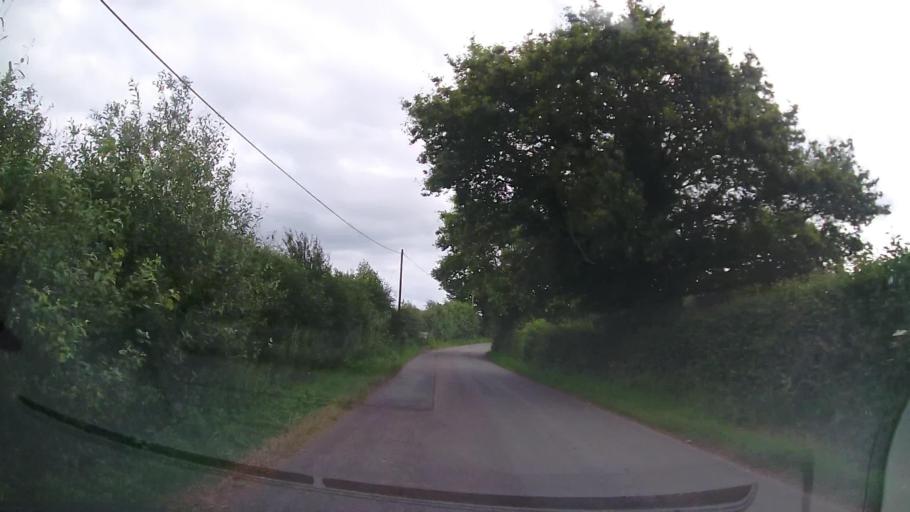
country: GB
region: England
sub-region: Shropshire
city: Whitchurch
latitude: 52.9254
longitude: -2.7238
